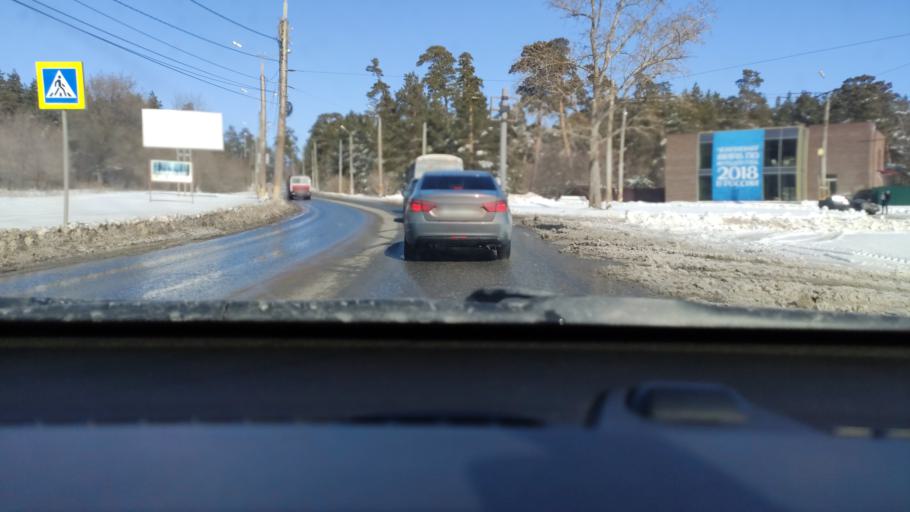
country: RU
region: Samara
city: Tol'yatti
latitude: 53.4768
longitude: 49.3469
